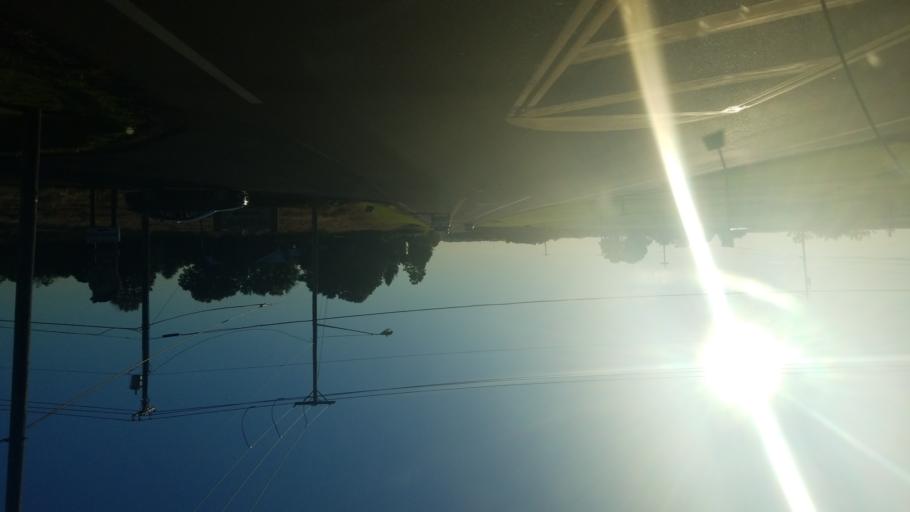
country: US
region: Ohio
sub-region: Mahoning County
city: Sebring
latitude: 40.9015
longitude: -81.0187
